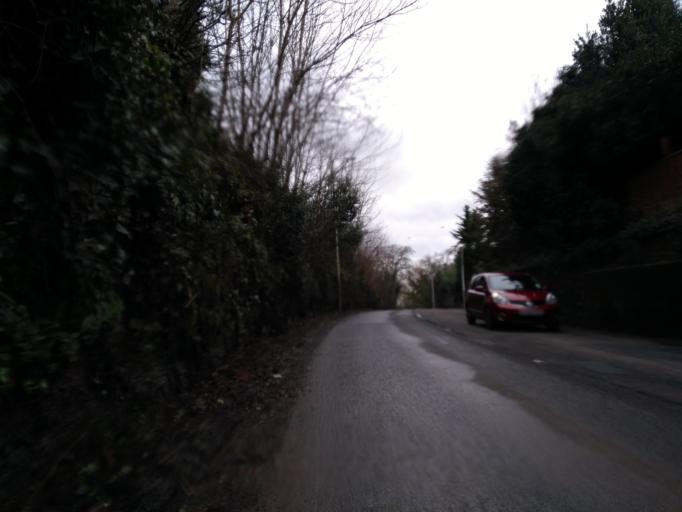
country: GB
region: England
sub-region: Devon
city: Crediton
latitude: 50.7714
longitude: -3.5919
